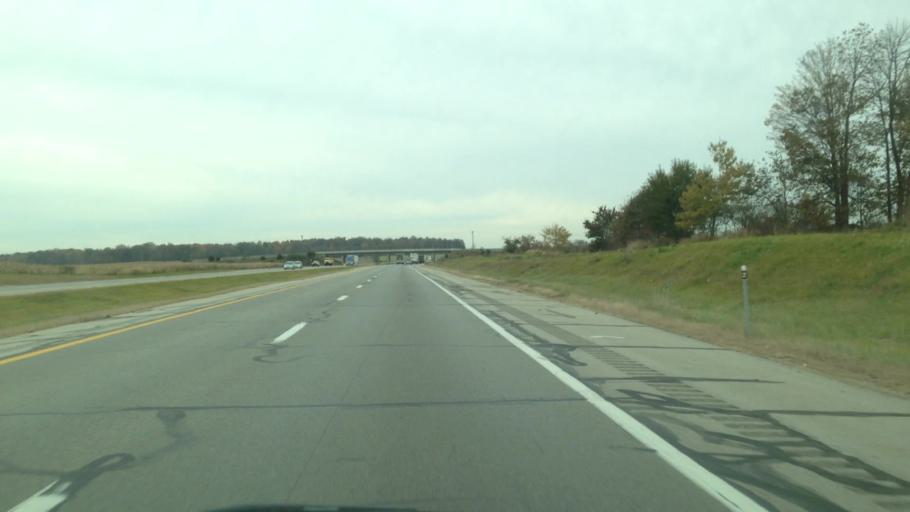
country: US
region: Ohio
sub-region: Williams County
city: Montpelier
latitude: 41.6180
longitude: -84.6687
